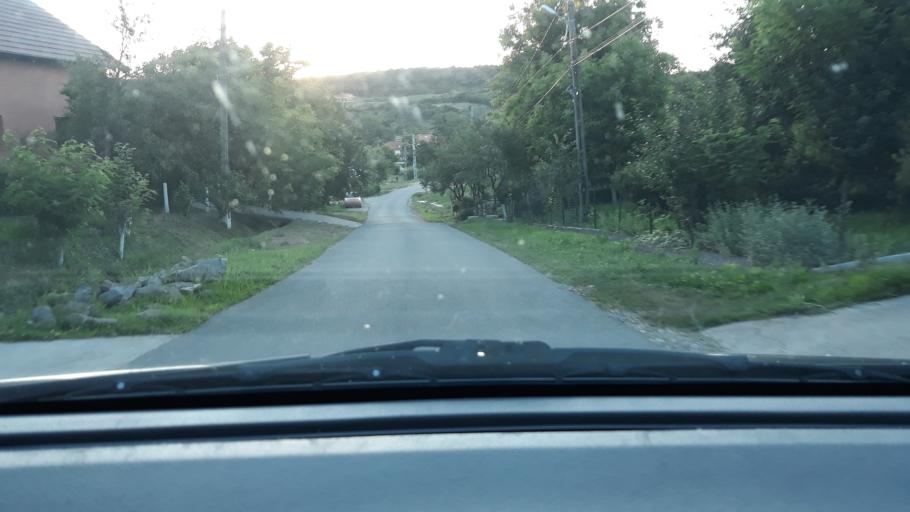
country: RO
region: Bihor
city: Hidiselu de Sus
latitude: 46.9403
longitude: 22.0208
